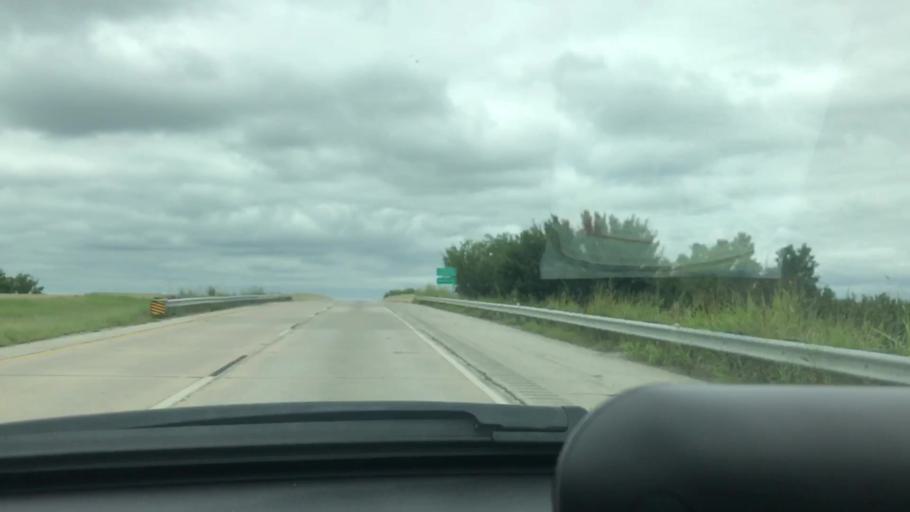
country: US
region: Oklahoma
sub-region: Wagoner County
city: Wagoner
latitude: 35.8839
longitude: -95.4029
